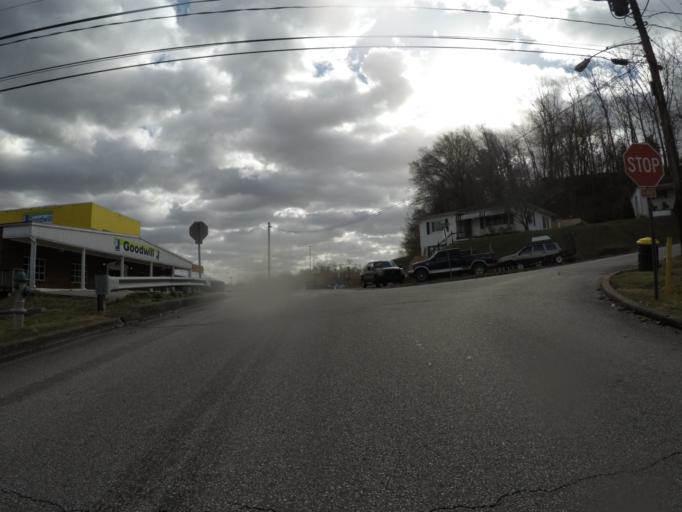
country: US
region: West Virginia
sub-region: Cabell County
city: Huntington
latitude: 38.4111
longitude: -82.3869
